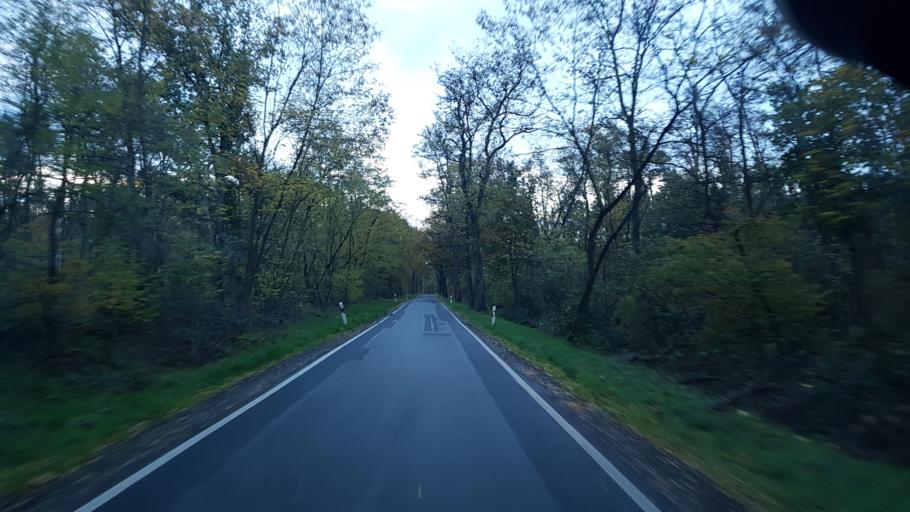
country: DE
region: Brandenburg
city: Muhlberg
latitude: 51.4848
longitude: 13.2303
